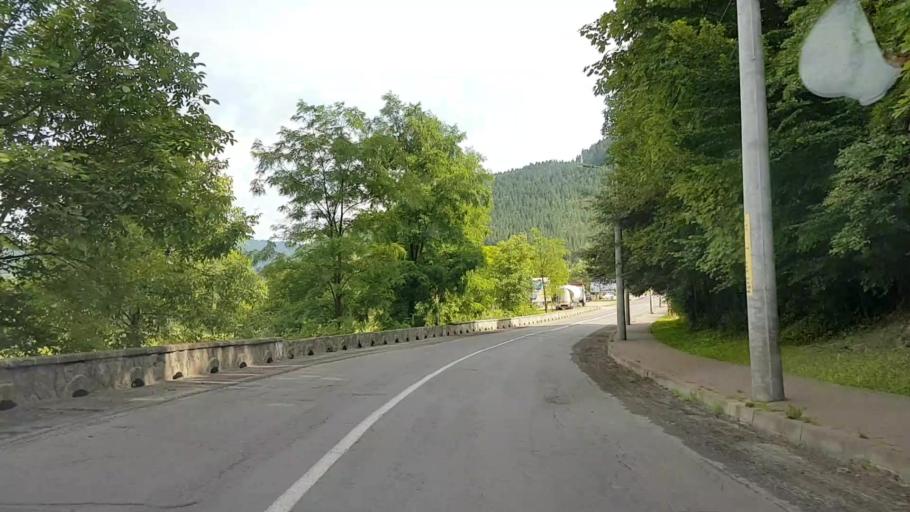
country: RO
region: Neamt
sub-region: Comuna Bicaz
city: Dodeni
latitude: 46.9164
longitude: 26.0853
